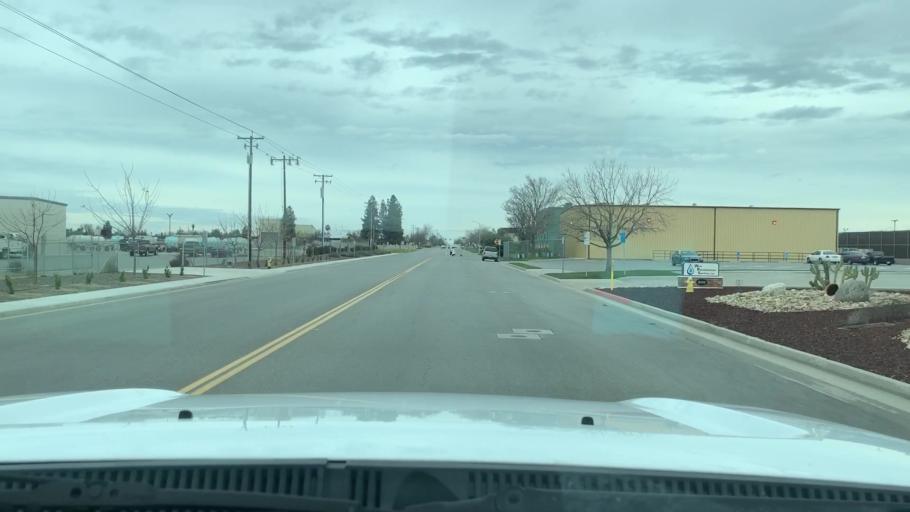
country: US
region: California
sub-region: Kern County
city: Shafter
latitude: 35.4944
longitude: -119.2606
